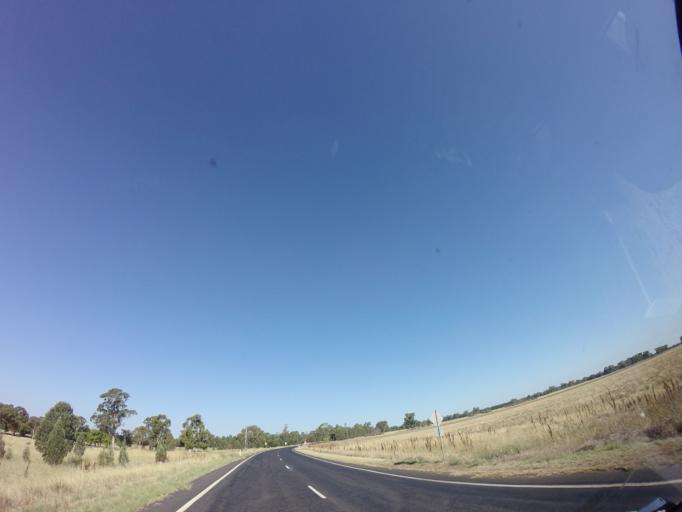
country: AU
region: New South Wales
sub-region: Gilgandra
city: Gilgandra
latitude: -31.7045
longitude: 148.6278
